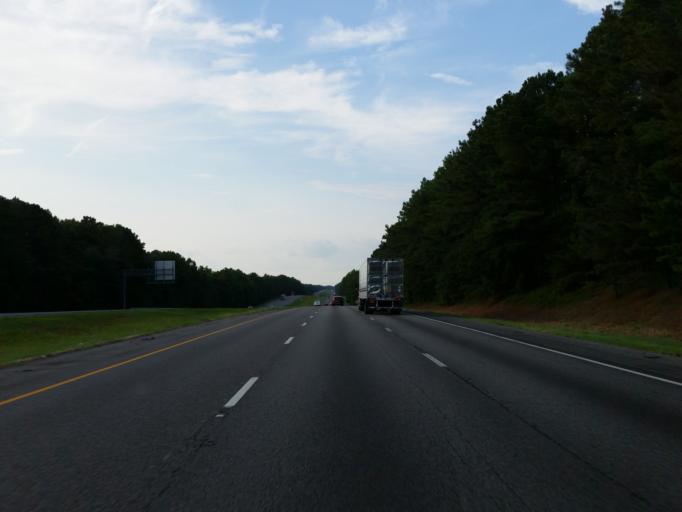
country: US
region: Georgia
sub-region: Dooly County
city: Unadilla
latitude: 32.3516
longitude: -83.7684
